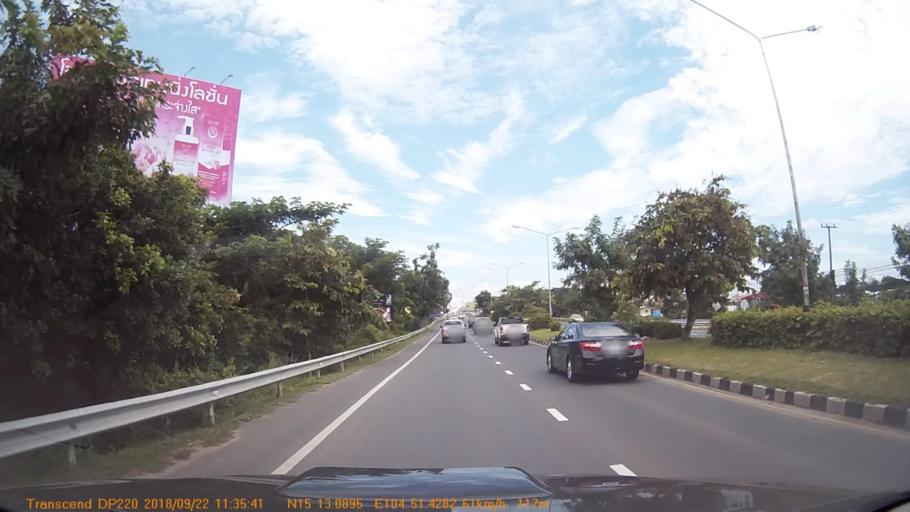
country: TH
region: Changwat Ubon Ratchathani
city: Ubon Ratchathani
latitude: 15.2182
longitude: 104.8571
